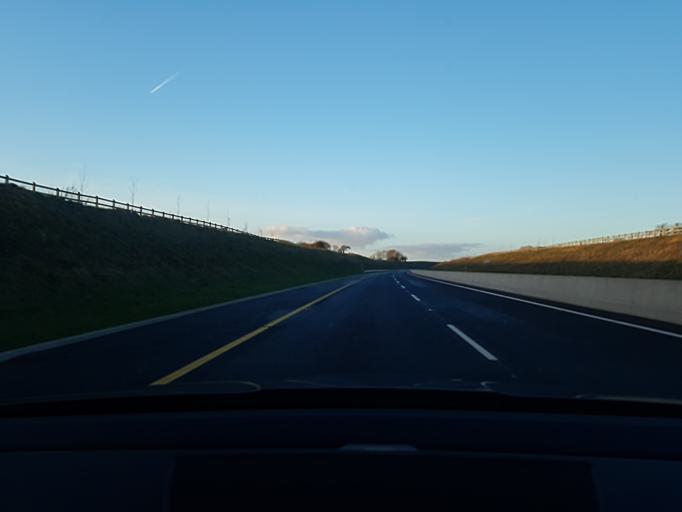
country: IE
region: Connaught
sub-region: County Galway
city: Tuam
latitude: 53.4403
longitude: -8.8480
